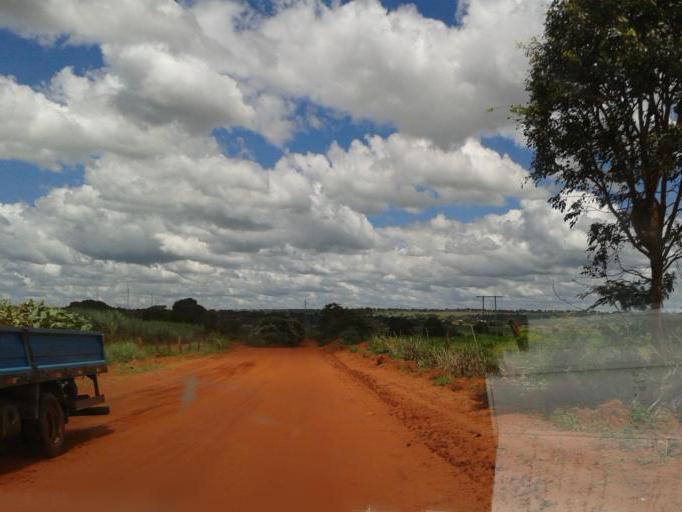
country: BR
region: Minas Gerais
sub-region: Santa Vitoria
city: Santa Vitoria
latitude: -18.8407
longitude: -50.1010
